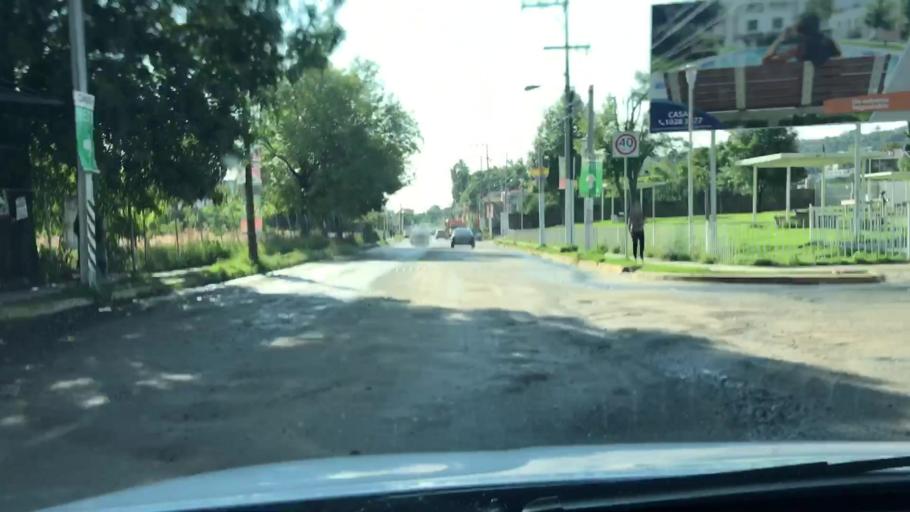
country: MX
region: Jalisco
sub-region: Tlajomulco de Zuniga
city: Palomar
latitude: 20.6262
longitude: -103.4782
